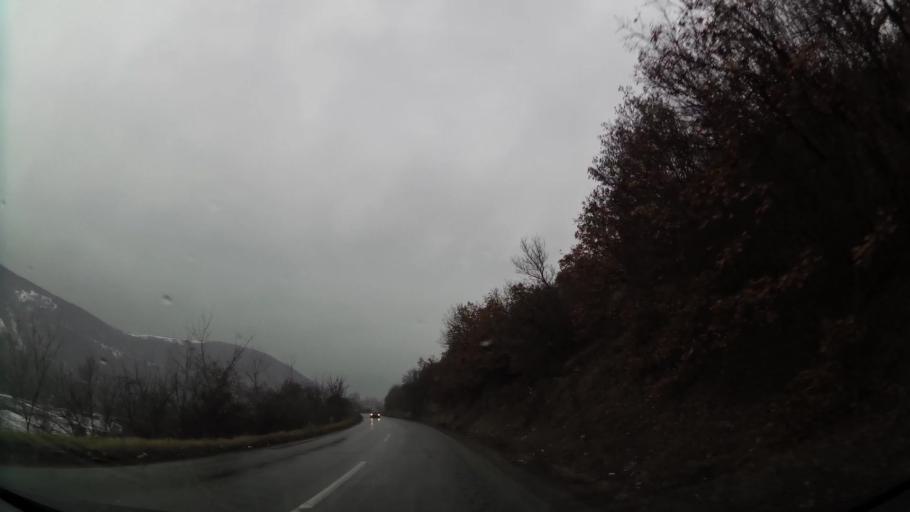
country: XK
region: Ferizaj
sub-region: Hani i Elezit
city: Hani i Elezit
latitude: 42.1328
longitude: 21.3113
